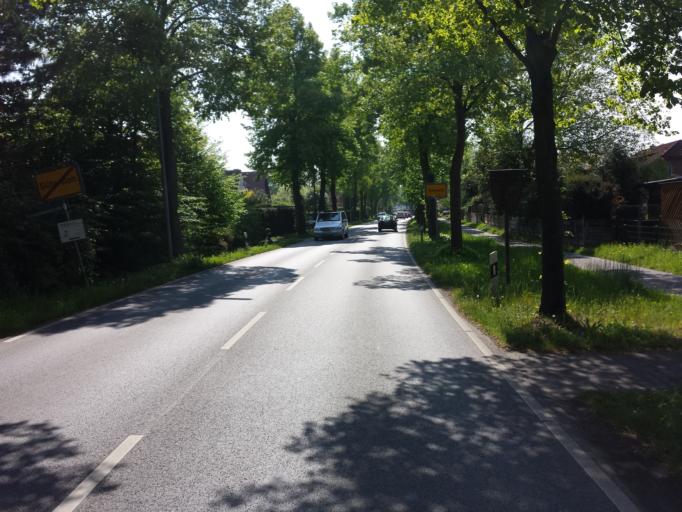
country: DE
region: North Rhine-Westphalia
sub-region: Regierungsbezirk Detmold
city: Guetersloh
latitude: 51.8852
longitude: 8.3906
